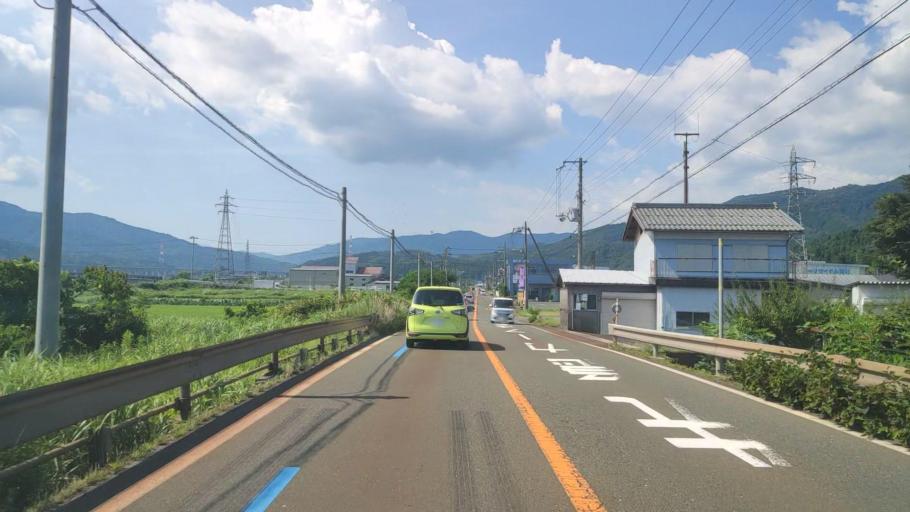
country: JP
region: Shiga Prefecture
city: Nagahama
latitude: 35.5166
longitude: 136.1645
